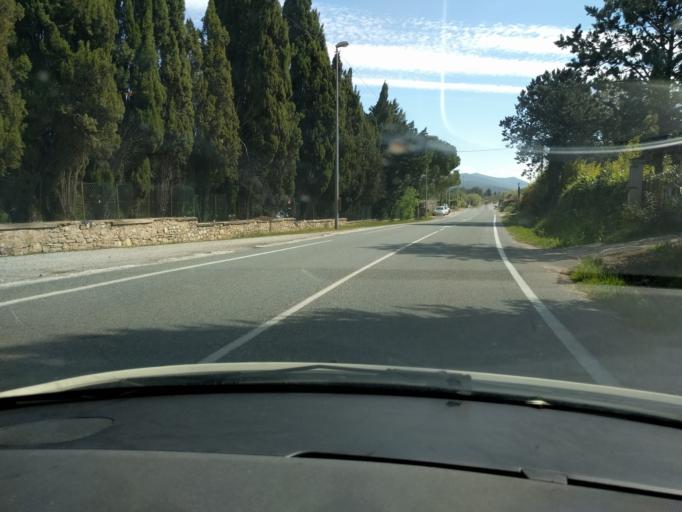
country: FR
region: Provence-Alpes-Cote d'Azur
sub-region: Departement du Var
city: Pierrefeu-du-Var
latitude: 43.2315
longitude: 6.1507
